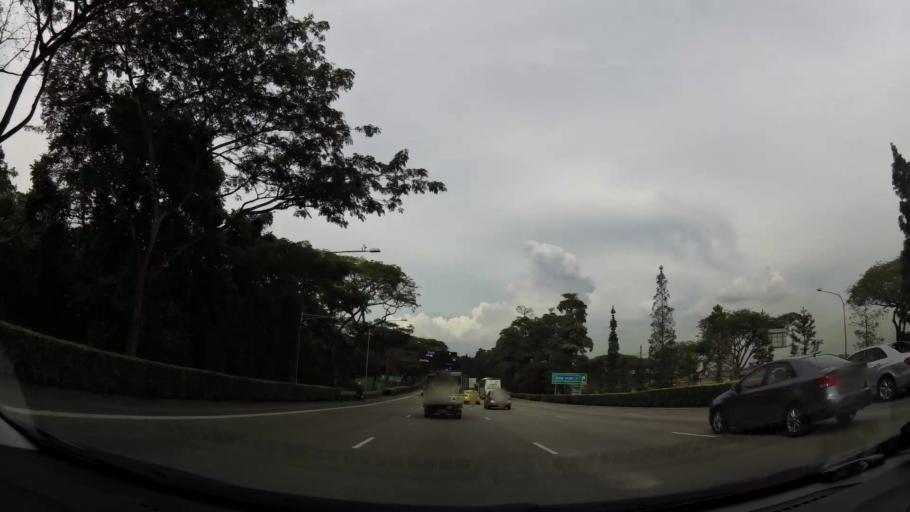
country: MY
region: Johor
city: Johor Bahru
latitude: 1.3591
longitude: 103.7012
